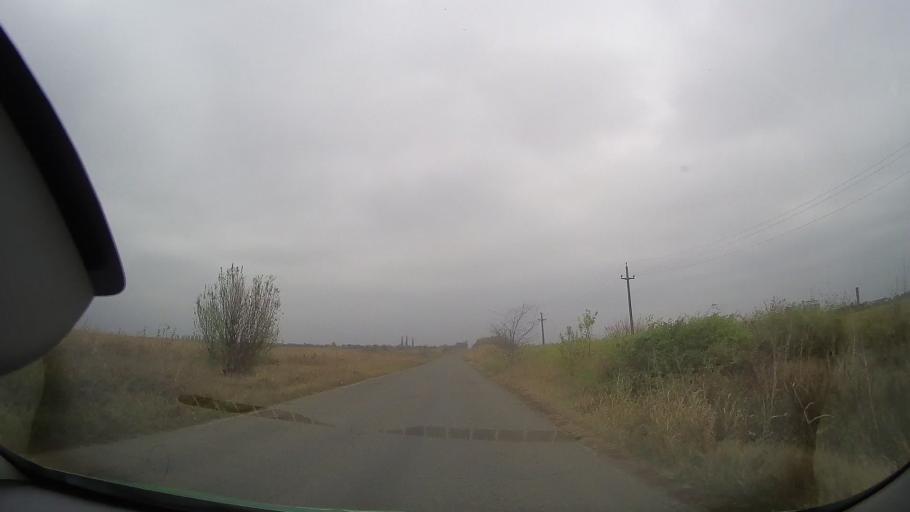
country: RO
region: Buzau
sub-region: Comuna Glodeanu-Silistea
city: Glodeanu-Silistea
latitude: 44.8159
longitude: 26.8447
